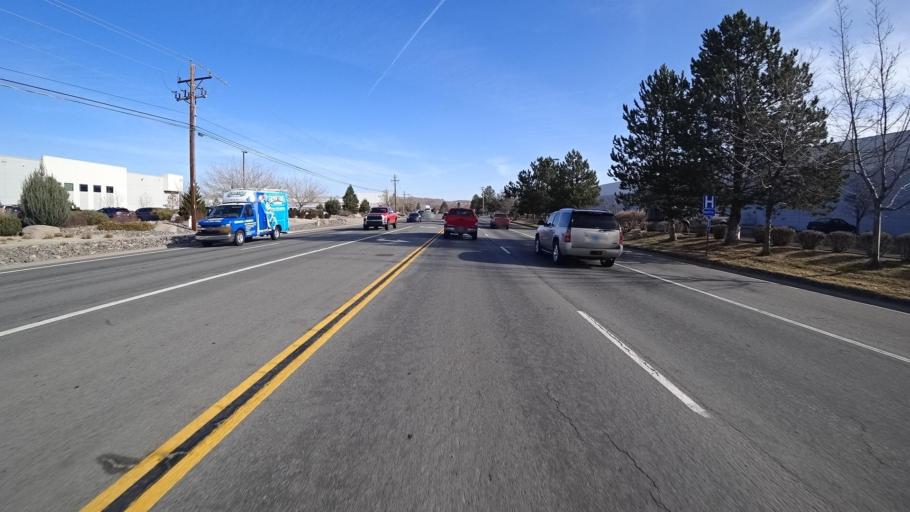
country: US
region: Nevada
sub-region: Washoe County
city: Sparks
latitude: 39.5377
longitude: -119.7036
